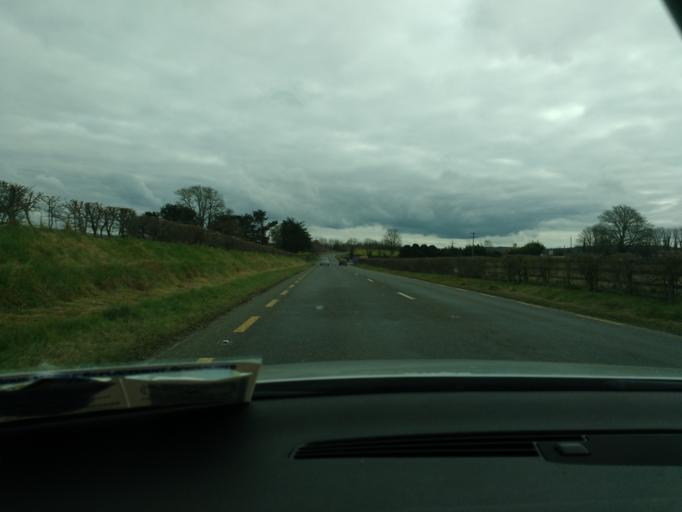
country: IE
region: Leinster
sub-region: Kilkenny
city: Ballyragget
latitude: 52.7180
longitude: -7.3392
